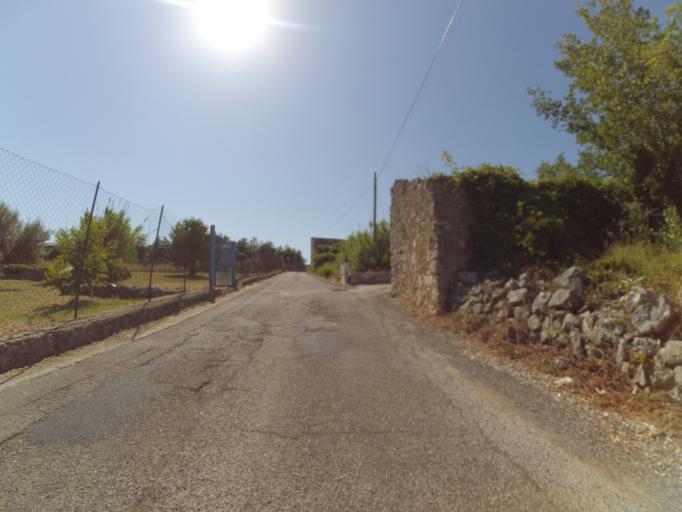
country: IT
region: Latium
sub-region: Provincia di Latina
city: Gaeta
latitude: 41.2255
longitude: 13.5451
